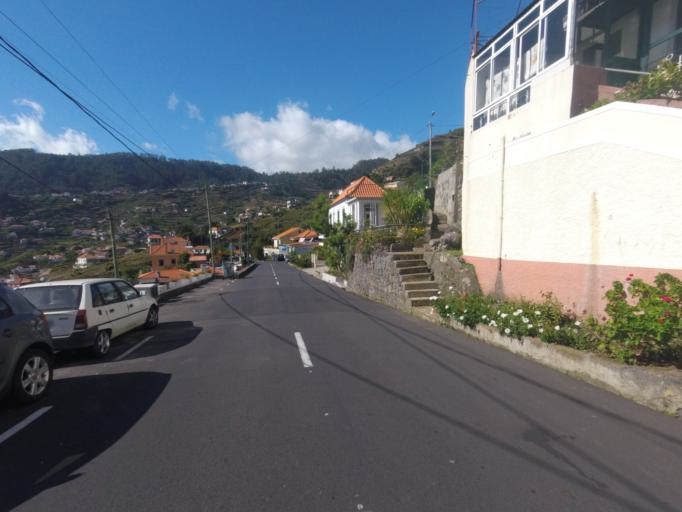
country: PT
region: Madeira
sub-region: Ribeira Brava
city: Campanario
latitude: 32.6712
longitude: -17.0214
